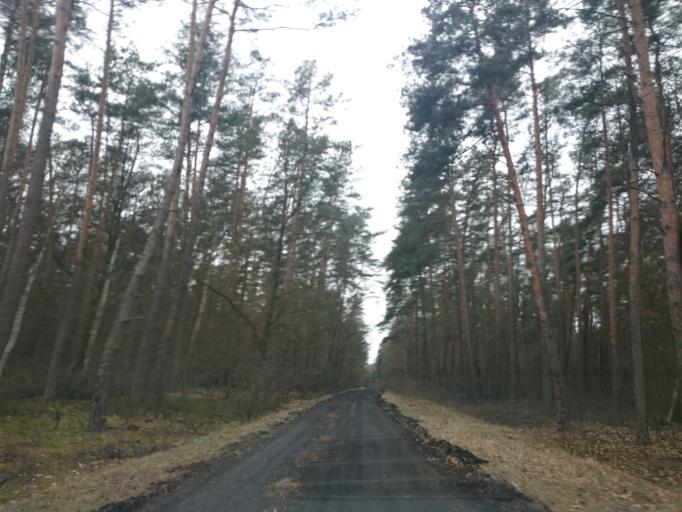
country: PL
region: Kujawsko-Pomorskie
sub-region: Powiat golubsko-dobrzynski
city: Ciechocin
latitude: 53.0756
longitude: 18.9152
